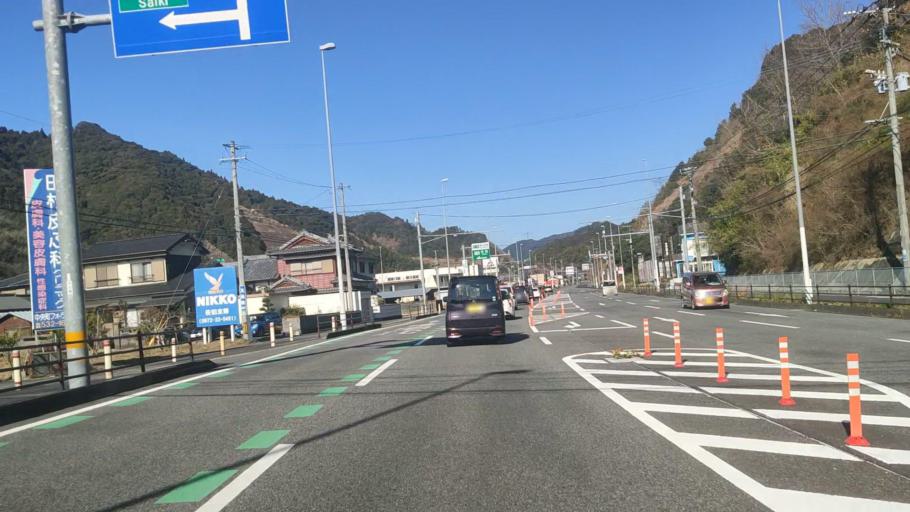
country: JP
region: Oita
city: Saiki
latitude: 32.9642
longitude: 131.8619
